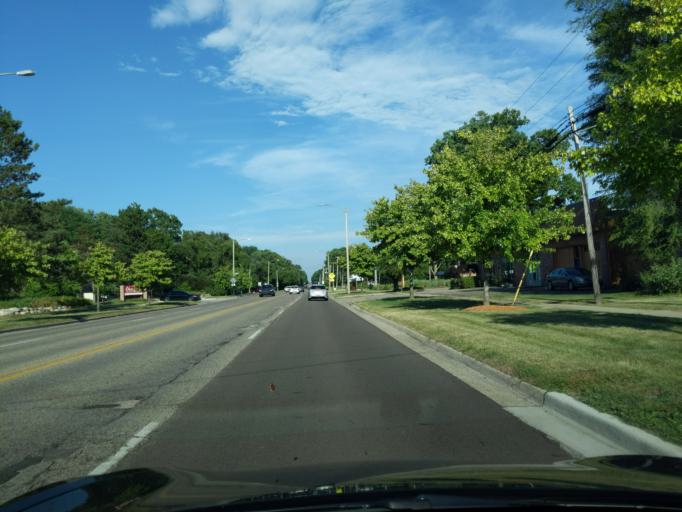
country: US
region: Michigan
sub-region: Ingham County
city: East Lansing
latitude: 42.7469
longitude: -84.4554
